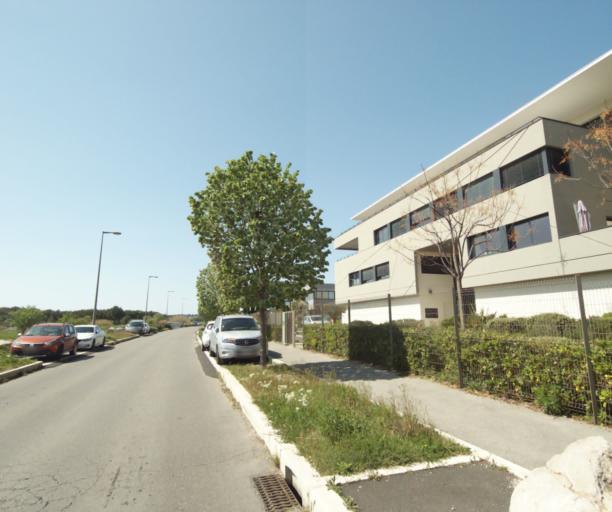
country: FR
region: Languedoc-Roussillon
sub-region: Departement de l'Herault
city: Grabels
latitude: 43.6434
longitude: 3.8270
